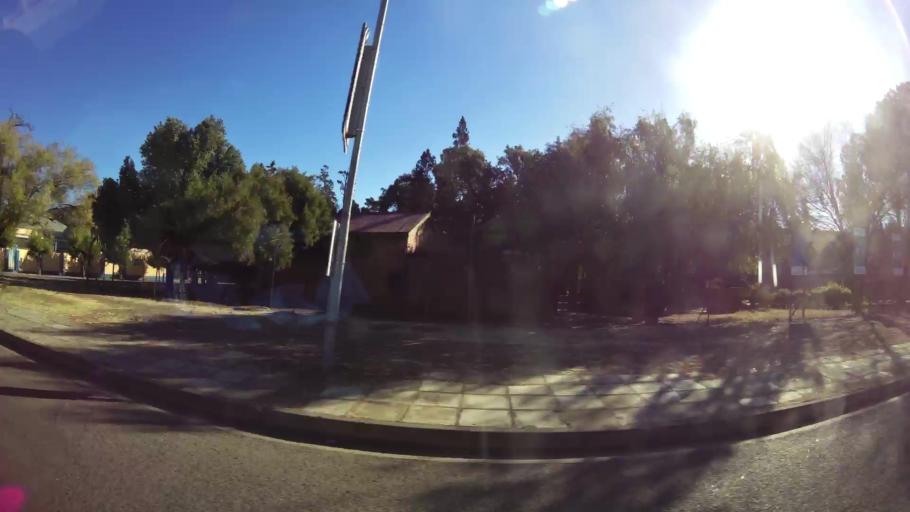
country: ZA
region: Northern Cape
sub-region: Frances Baard District Municipality
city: Kimberley
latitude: -28.7418
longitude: 24.7710
